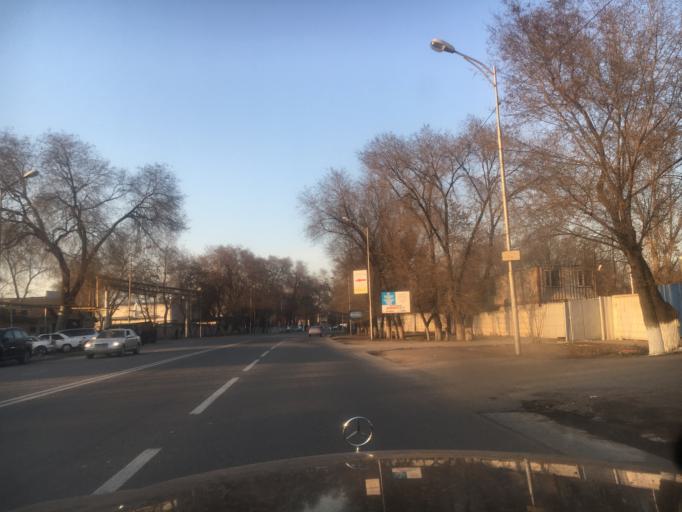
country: KZ
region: Almaty Oblysy
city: Pervomayskiy
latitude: 43.3611
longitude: 76.9817
